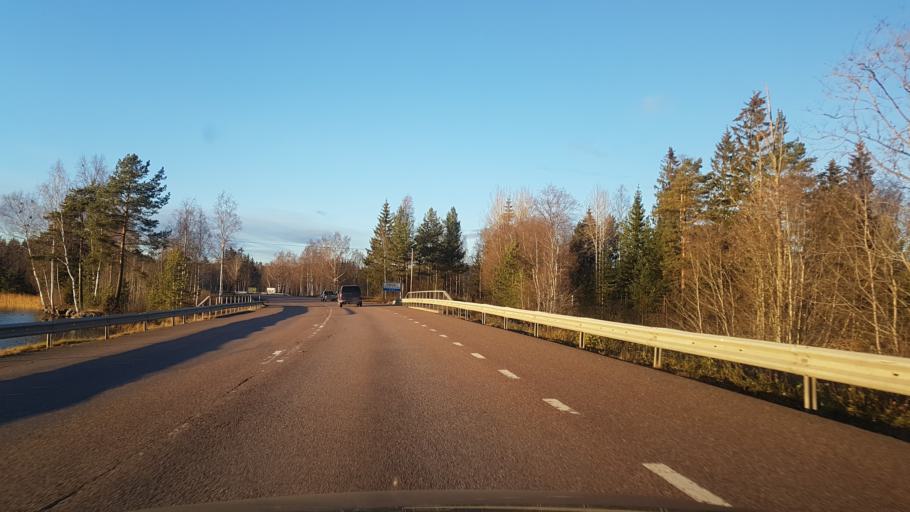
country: SE
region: Dalarna
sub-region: Faluns Kommun
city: Bjursas
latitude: 60.7180
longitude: 15.4580
